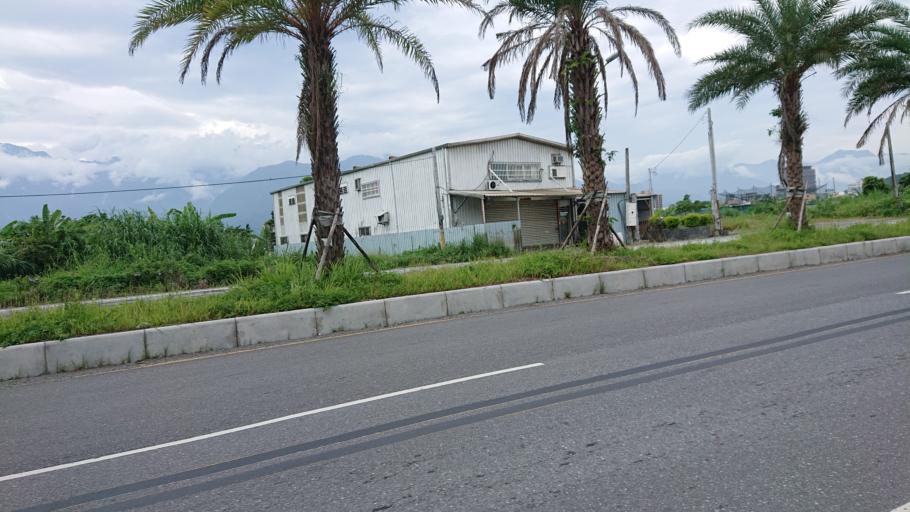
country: TW
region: Taiwan
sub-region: Hualien
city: Hualian
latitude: 23.9654
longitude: 121.6075
